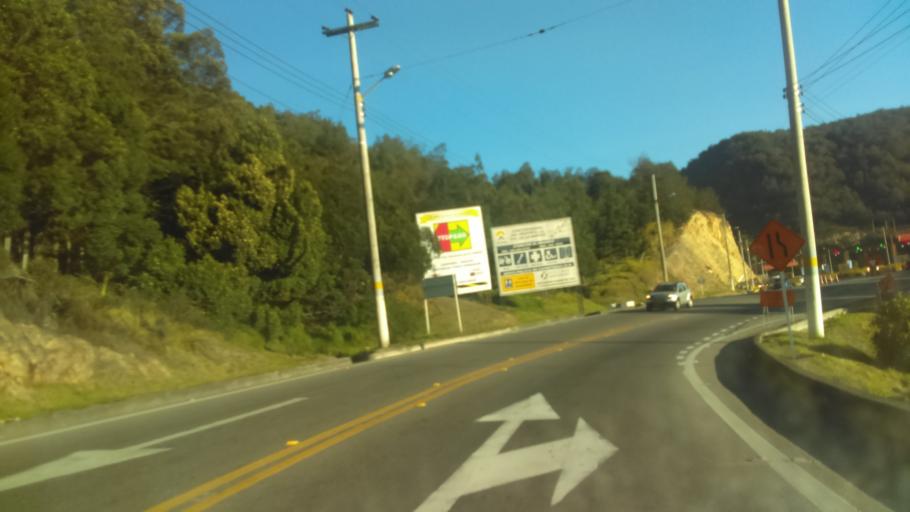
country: CO
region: Cundinamarca
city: San Antonio del Tequendama
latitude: 4.6368
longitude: -74.2945
